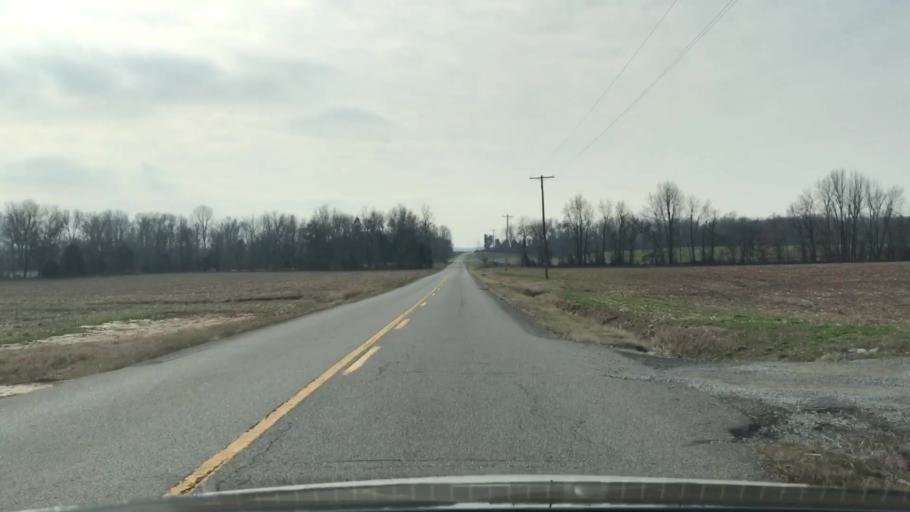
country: US
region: Kentucky
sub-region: Webster County
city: Sebree
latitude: 37.5047
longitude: -87.4310
